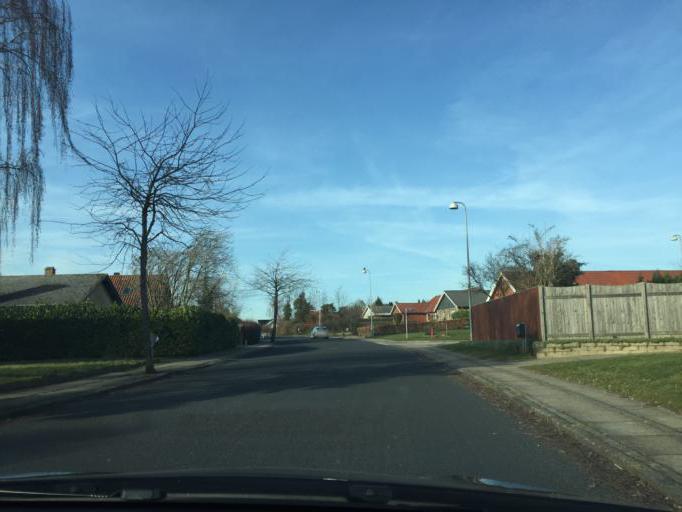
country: DK
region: South Denmark
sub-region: Odense Kommune
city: Odense
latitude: 55.3695
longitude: 10.3552
